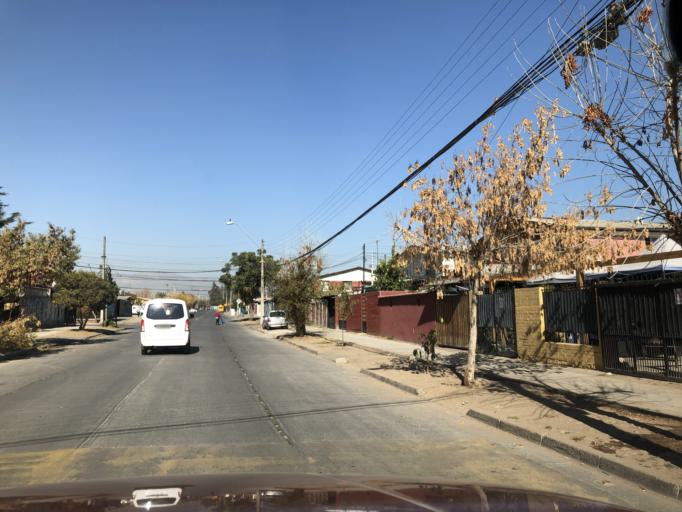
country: CL
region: Santiago Metropolitan
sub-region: Provincia de Cordillera
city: Puente Alto
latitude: -33.5653
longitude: -70.5794
